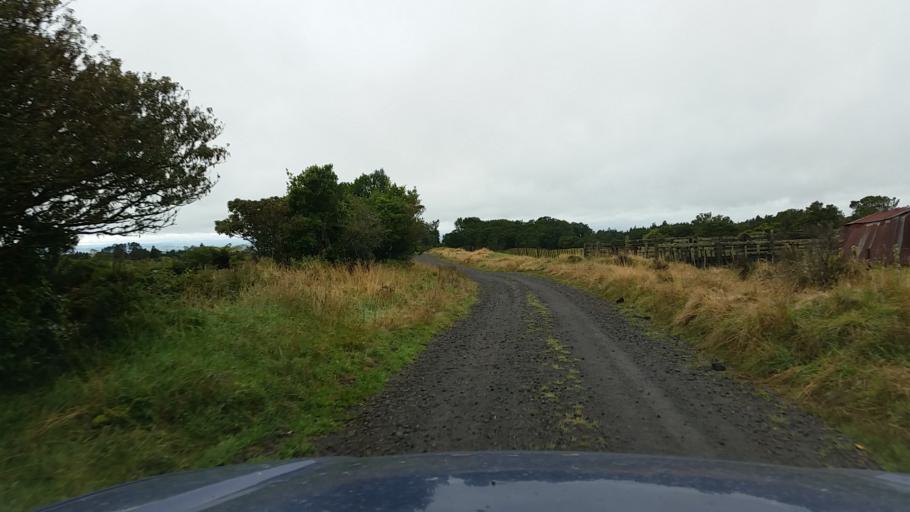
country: NZ
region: Taranaki
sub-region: South Taranaki District
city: Eltham
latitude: -39.3021
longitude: 174.1895
